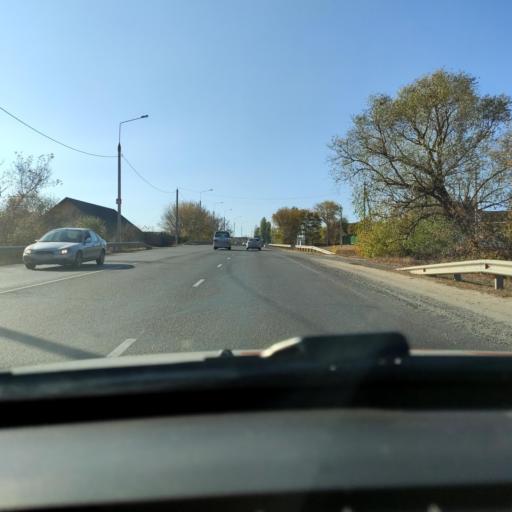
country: RU
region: Voronezj
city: Semiluki
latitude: 51.7266
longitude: 39.0462
